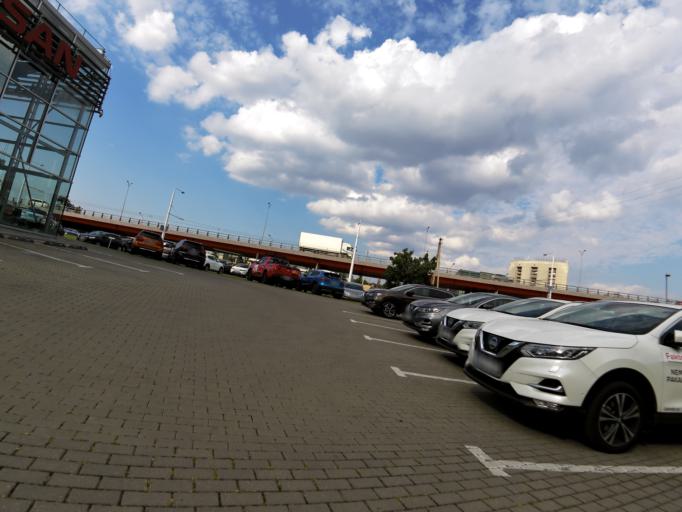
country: LT
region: Vilnius County
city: Vilkpede
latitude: 54.6685
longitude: 25.2355
